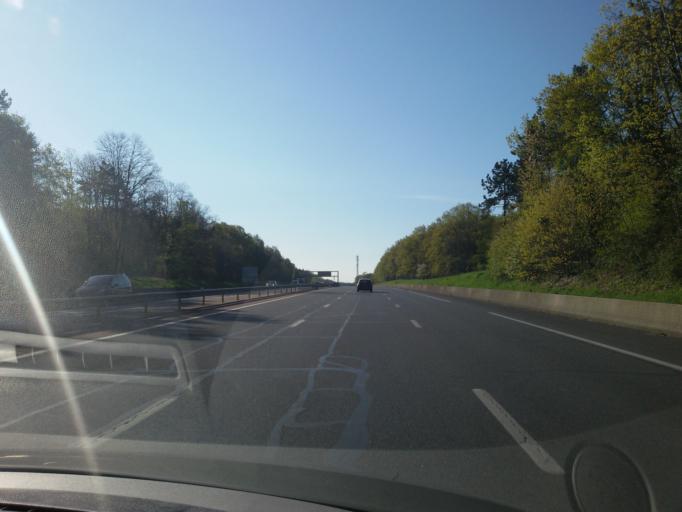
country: FR
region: Ile-de-France
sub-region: Departement de Seine-et-Marne
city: Bagneaux-sur-Loing
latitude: 48.2527
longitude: 2.7327
